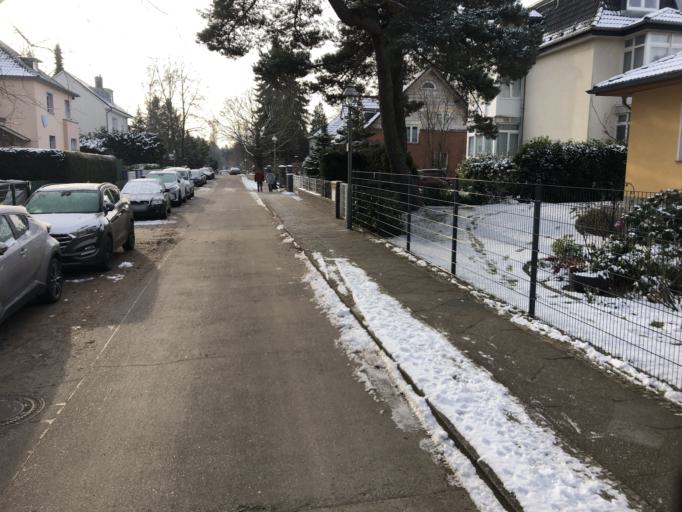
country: DE
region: Berlin
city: Hermsdorf
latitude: 52.6257
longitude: 13.3082
